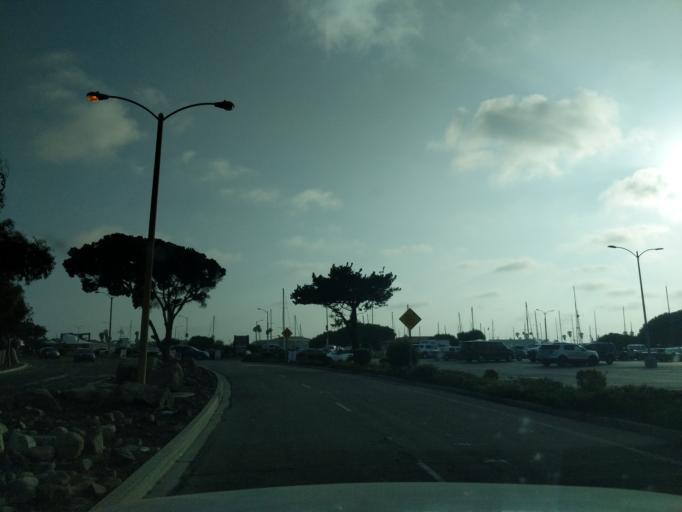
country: US
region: California
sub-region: Ventura County
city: Ventura
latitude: 34.2432
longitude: -119.2601
